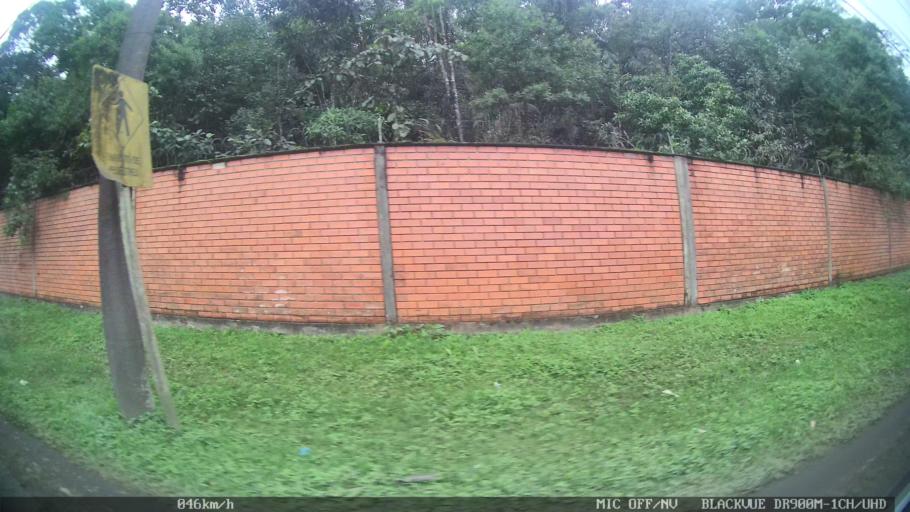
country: BR
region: Santa Catarina
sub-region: Joinville
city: Joinville
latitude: -26.2499
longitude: -48.8764
